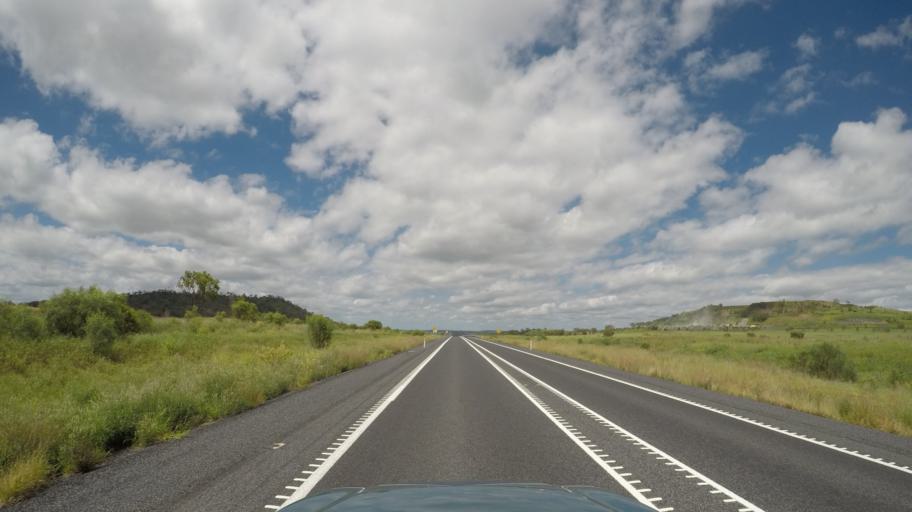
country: AU
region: Queensland
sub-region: Toowoomba
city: Westbrook
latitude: -27.5530
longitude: 151.8264
